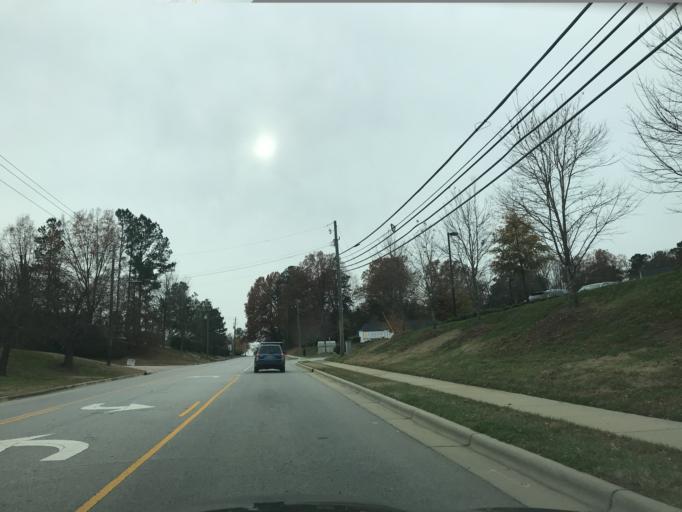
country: US
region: North Carolina
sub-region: Wake County
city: Raleigh
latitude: 35.8528
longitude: -78.6037
